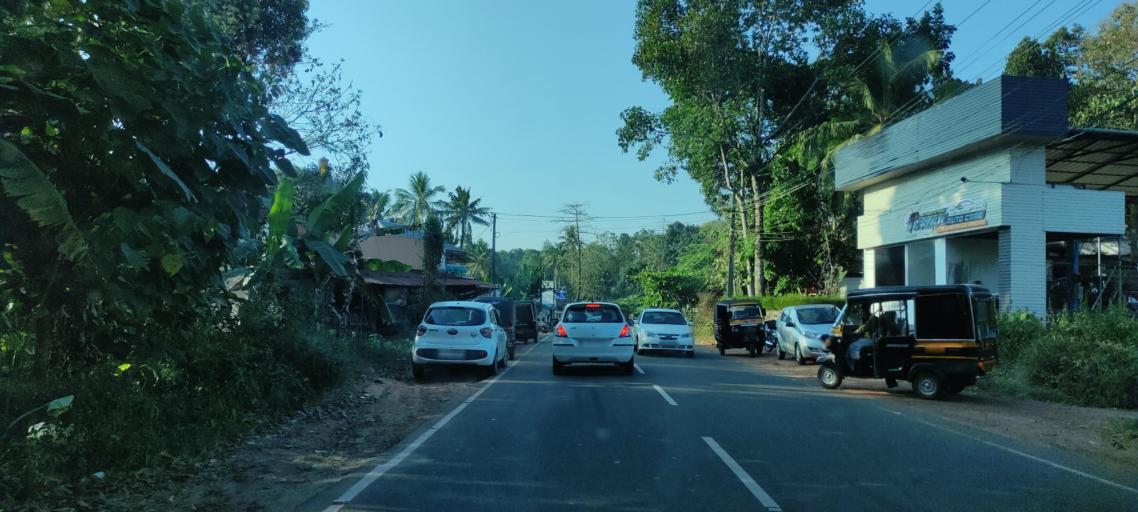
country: IN
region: Kerala
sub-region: Pattanamtitta
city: Adur
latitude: 9.1691
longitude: 76.6553
